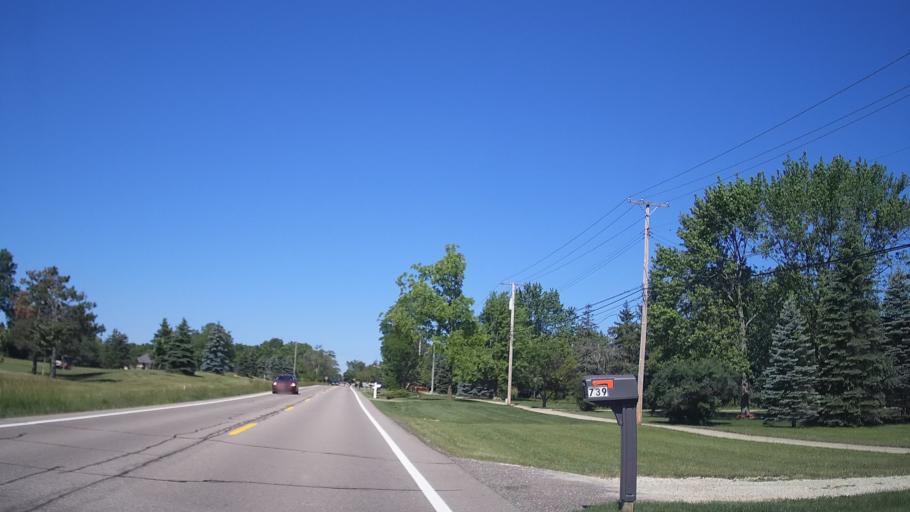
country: US
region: Michigan
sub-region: Oakland County
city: Troy
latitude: 42.6068
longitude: -83.1358
